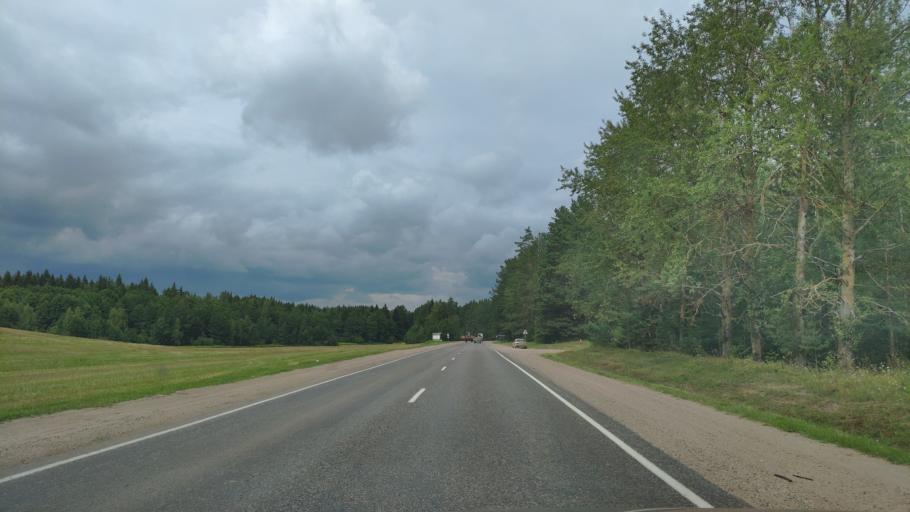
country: BY
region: Minsk
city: Zaslawye
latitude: 53.9683
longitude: 27.2461
